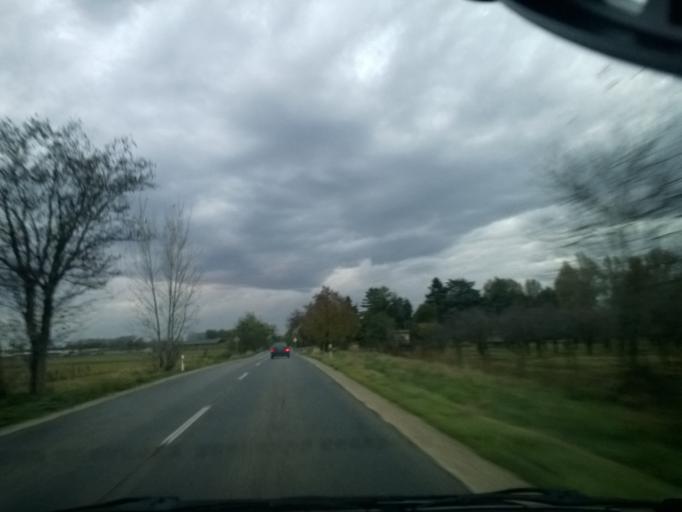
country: HU
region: Pest
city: Domsod
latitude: 47.0660
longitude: 19.0133
